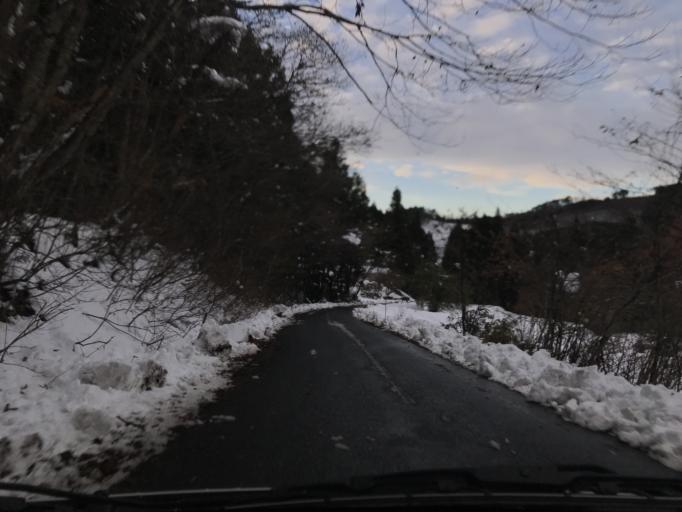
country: JP
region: Iwate
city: Mizusawa
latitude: 39.0441
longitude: 141.0201
